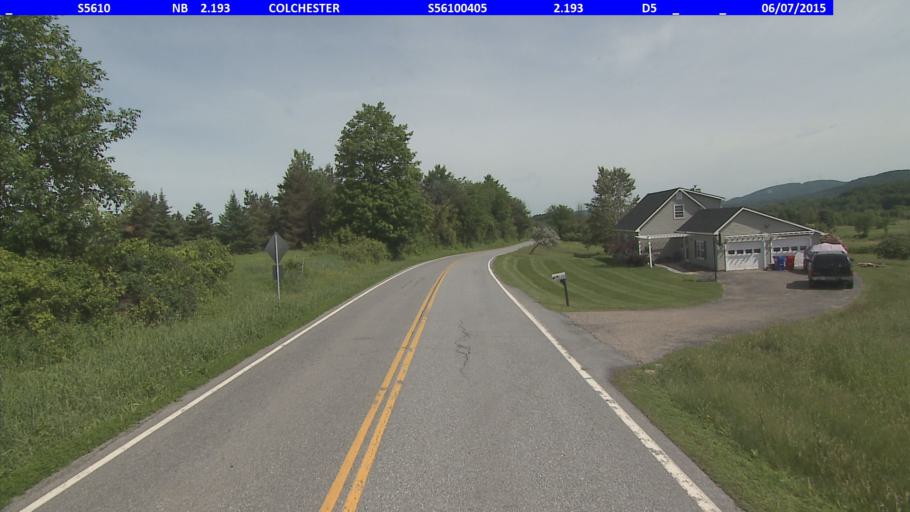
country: US
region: Vermont
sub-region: Chittenden County
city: Colchester
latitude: 44.5710
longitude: -73.1275
